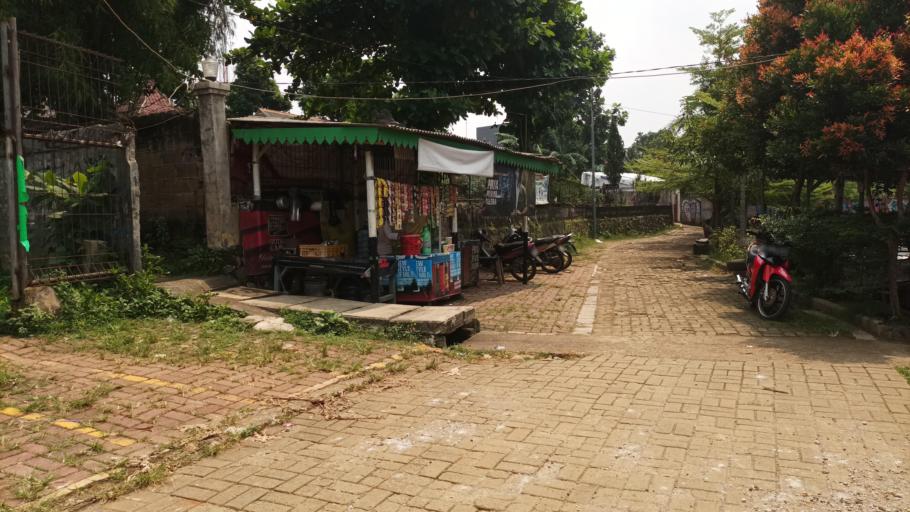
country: ID
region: West Java
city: Depok
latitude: -6.4217
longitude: 106.8587
